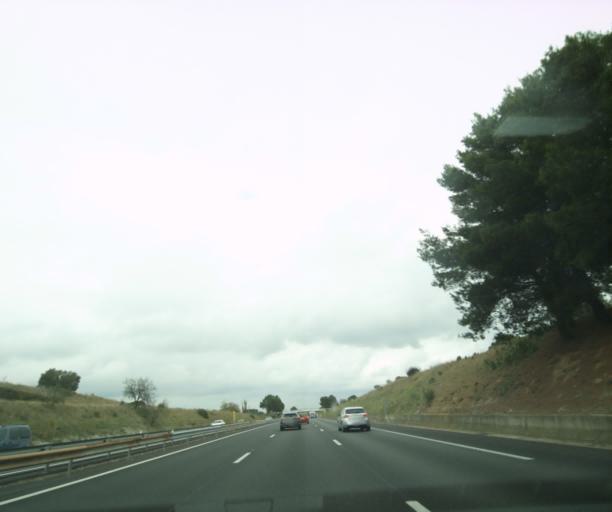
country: FR
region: Languedoc-Roussillon
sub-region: Departement de l'Herault
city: Meze
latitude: 43.4332
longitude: 3.5641
